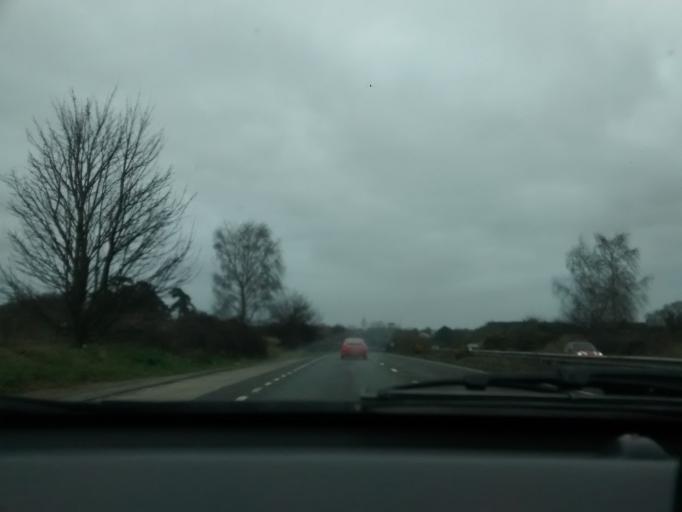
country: GB
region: England
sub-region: Suffolk
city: Kesgrave
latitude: 52.0396
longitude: 1.2620
